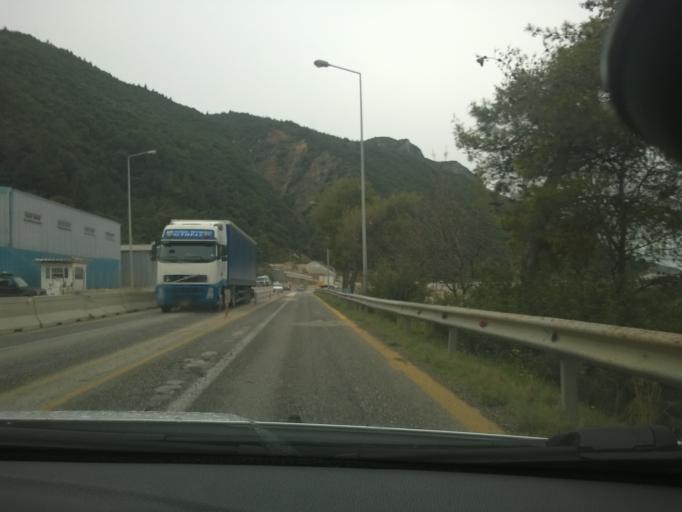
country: GR
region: West Greece
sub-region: Nomos Achaias
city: Kamarai
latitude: 38.3247
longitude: 21.9250
